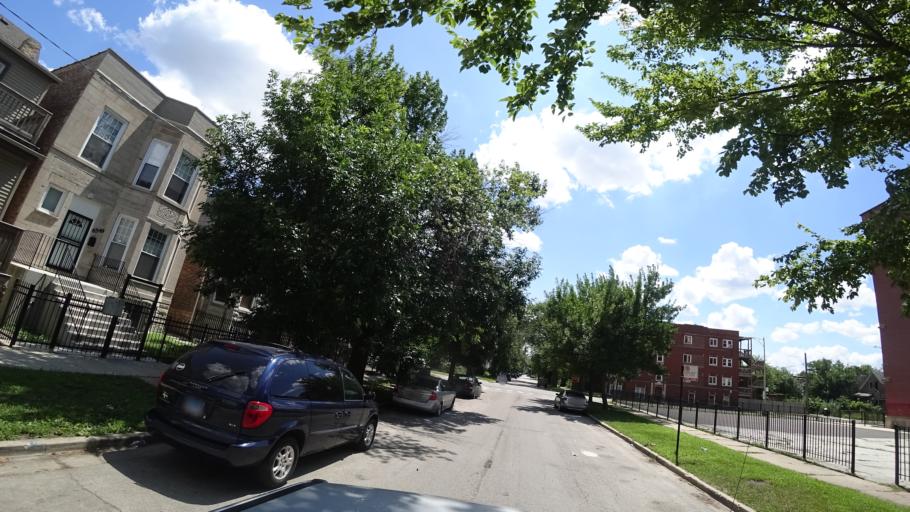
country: US
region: Illinois
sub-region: Cook County
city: Chicago
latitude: 41.7754
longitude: -87.6083
